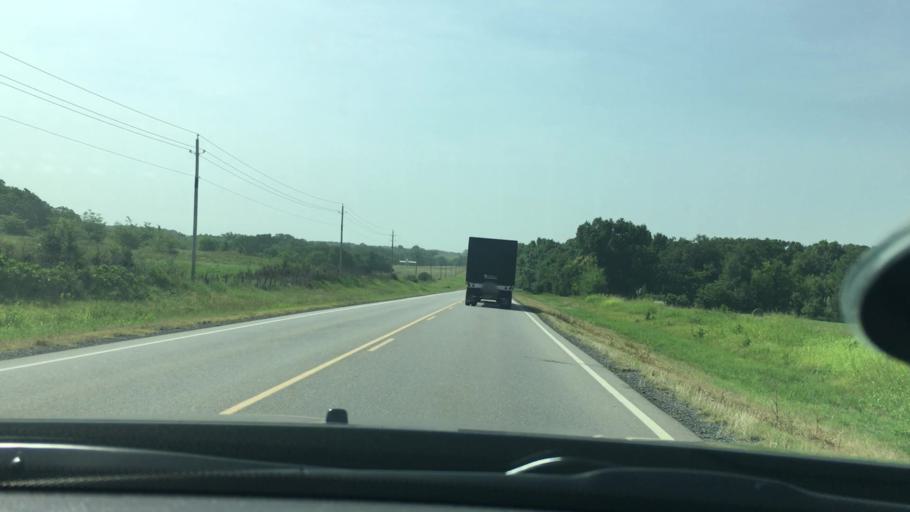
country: US
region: Oklahoma
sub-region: Atoka County
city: Atoka
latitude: 34.4147
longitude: -96.1859
